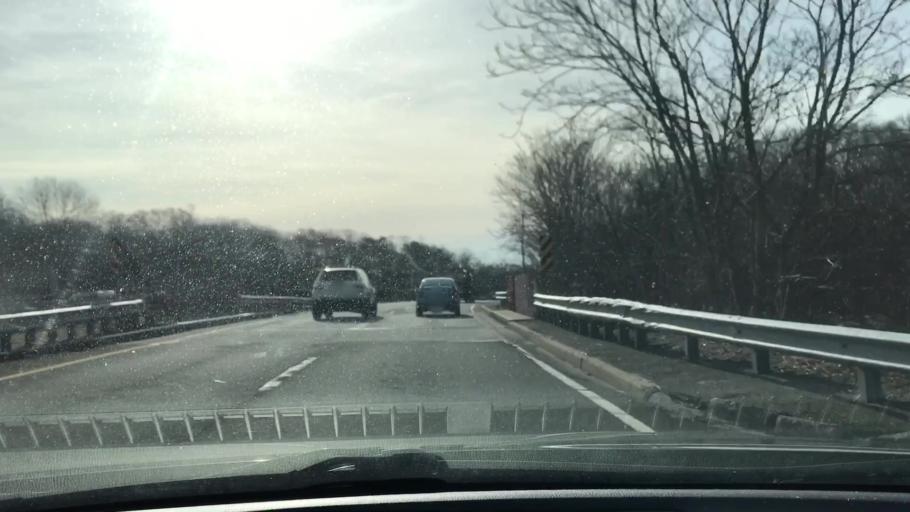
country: US
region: New York
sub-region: Suffolk County
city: Aquebogue
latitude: 40.9275
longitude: -72.6337
